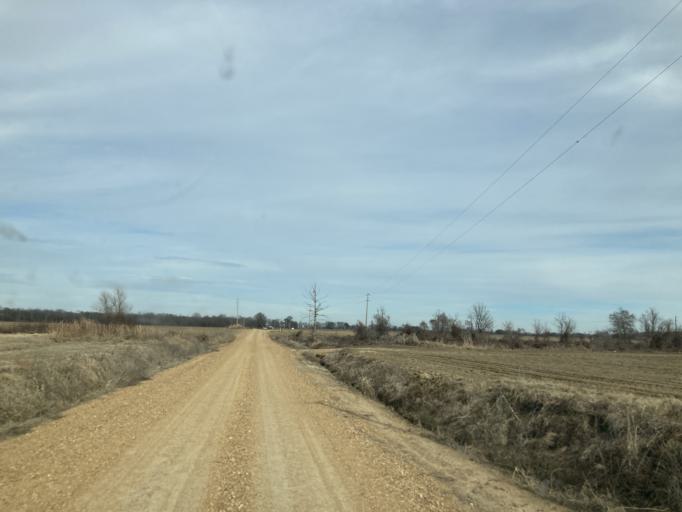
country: US
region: Mississippi
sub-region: Humphreys County
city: Belzoni
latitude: 33.0584
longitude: -90.6577
